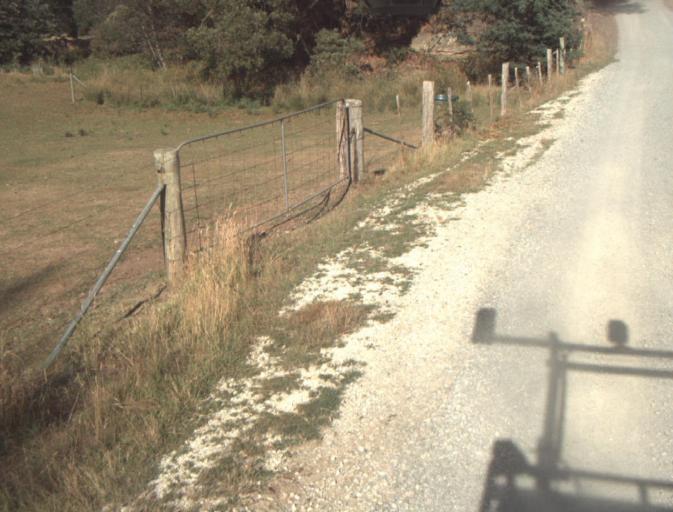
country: AU
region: Tasmania
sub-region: Launceston
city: Mayfield
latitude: -41.2875
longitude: 147.1946
